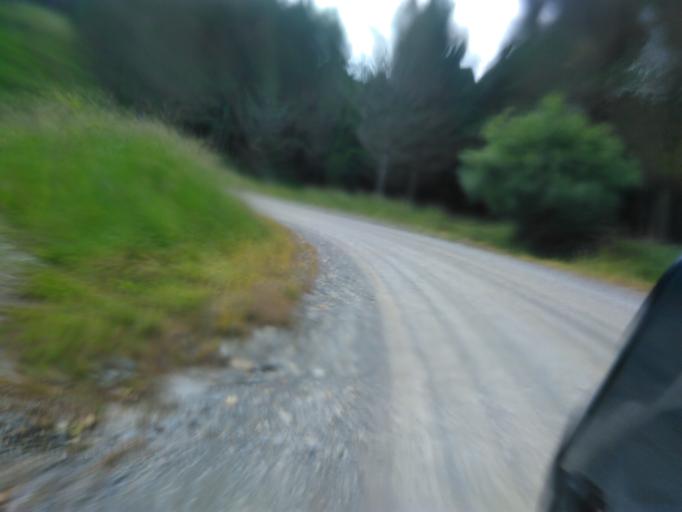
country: NZ
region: Gisborne
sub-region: Gisborne District
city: Gisborne
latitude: -38.0493
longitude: 178.1241
